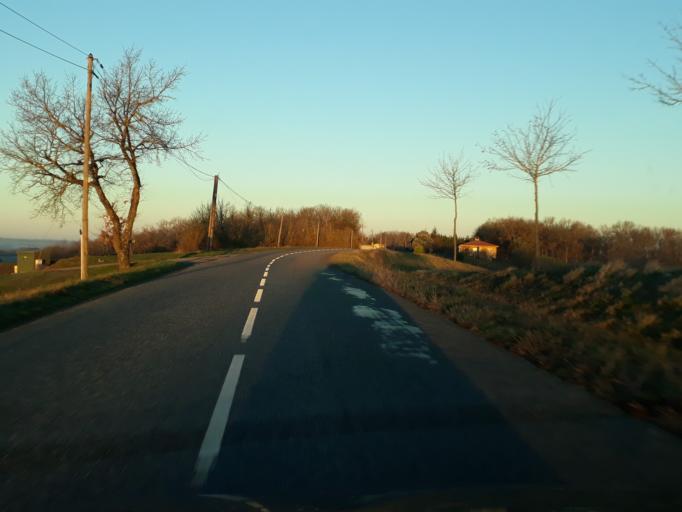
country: FR
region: Midi-Pyrenees
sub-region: Departement du Gers
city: Pavie
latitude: 43.6058
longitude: 0.6898
